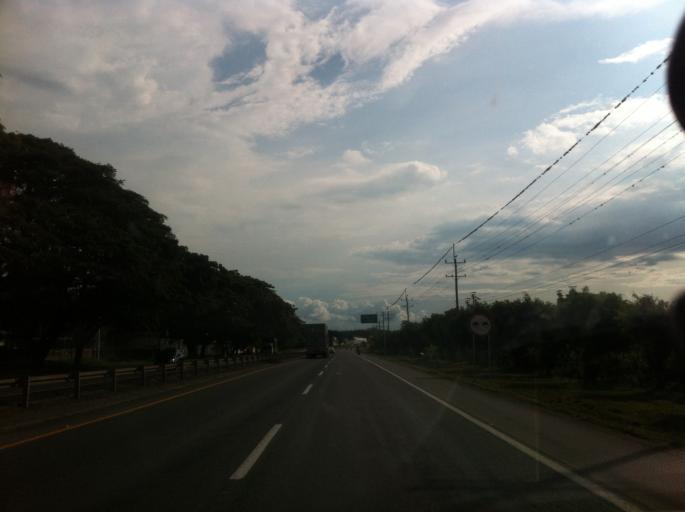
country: CO
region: Valle del Cauca
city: Buga
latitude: 3.9369
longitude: -76.2821
